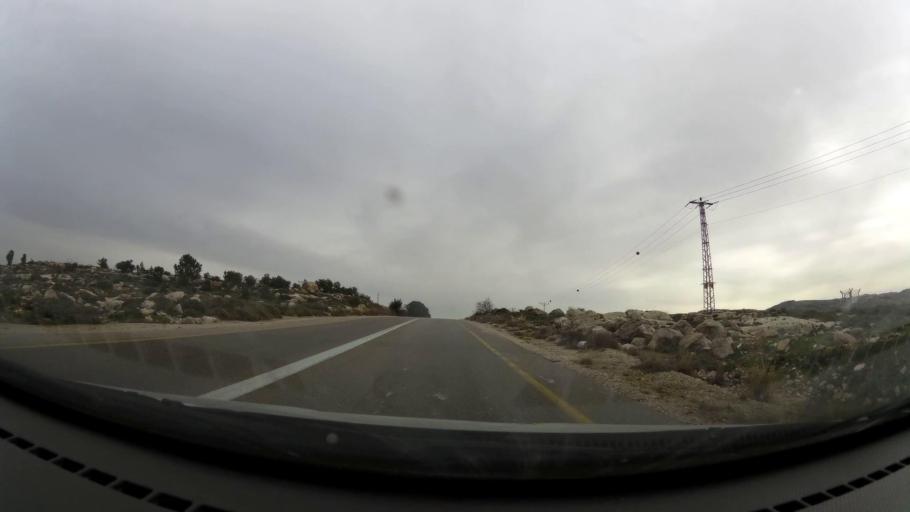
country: PS
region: West Bank
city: Surif
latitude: 31.6719
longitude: 35.0636
